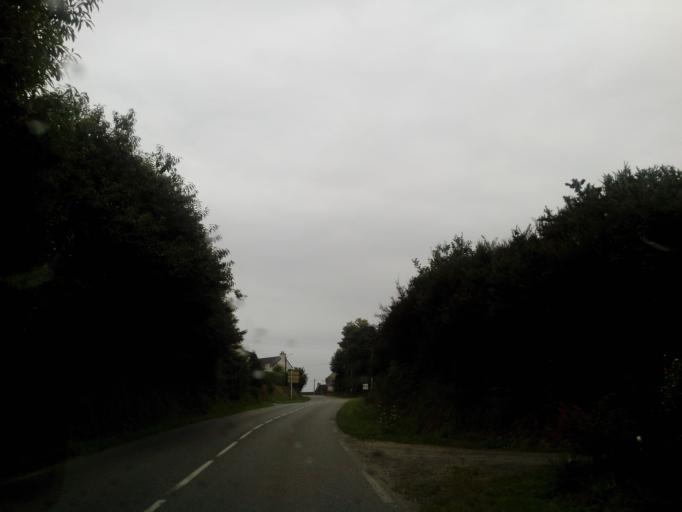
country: FR
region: Brittany
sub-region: Departement du Finistere
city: Tremeven
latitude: 47.9083
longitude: -3.5191
